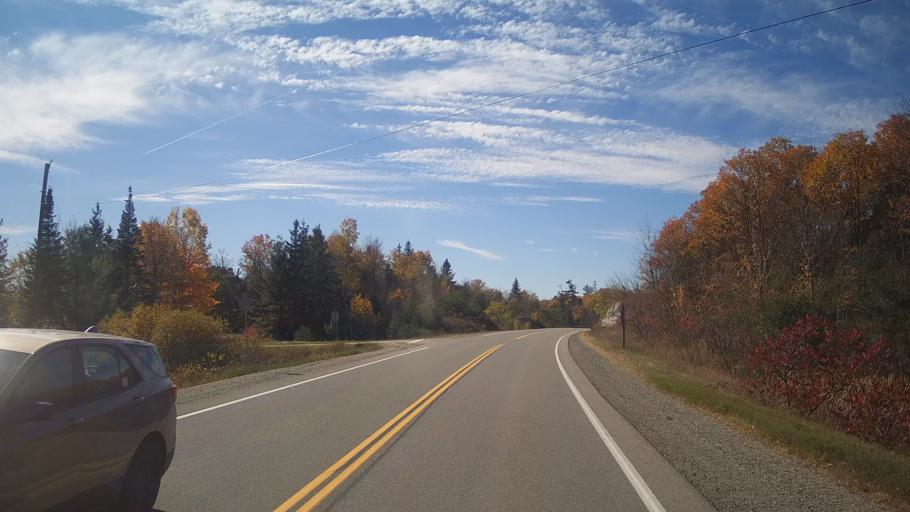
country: CA
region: Ontario
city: Perth
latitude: 44.8050
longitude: -76.6475
